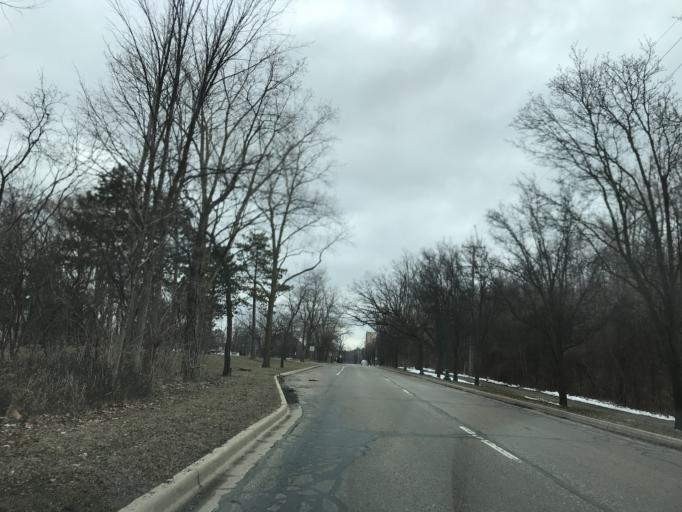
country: US
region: Michigan
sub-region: Oakland County
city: Bingham Farms
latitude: 42.4790
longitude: -83.2719
